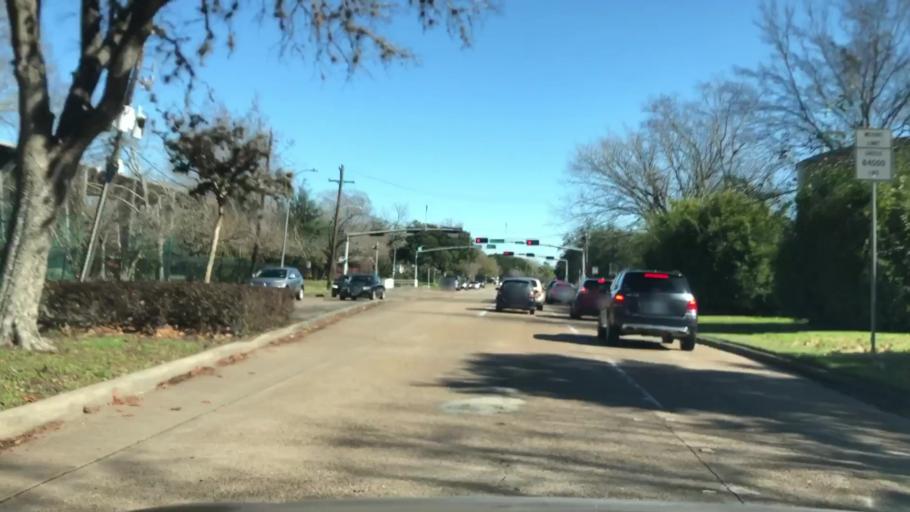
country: US
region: Texas
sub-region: Harris County
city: Bellaire
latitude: 29.6793
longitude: -95.4688
